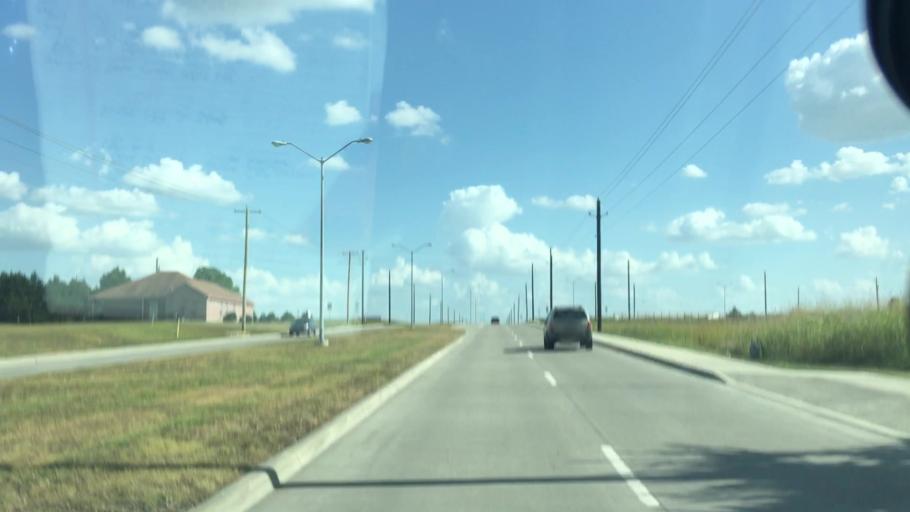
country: US
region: Texas
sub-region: Dallas County
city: Hutchins
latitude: 32.6384
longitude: -96.7519
